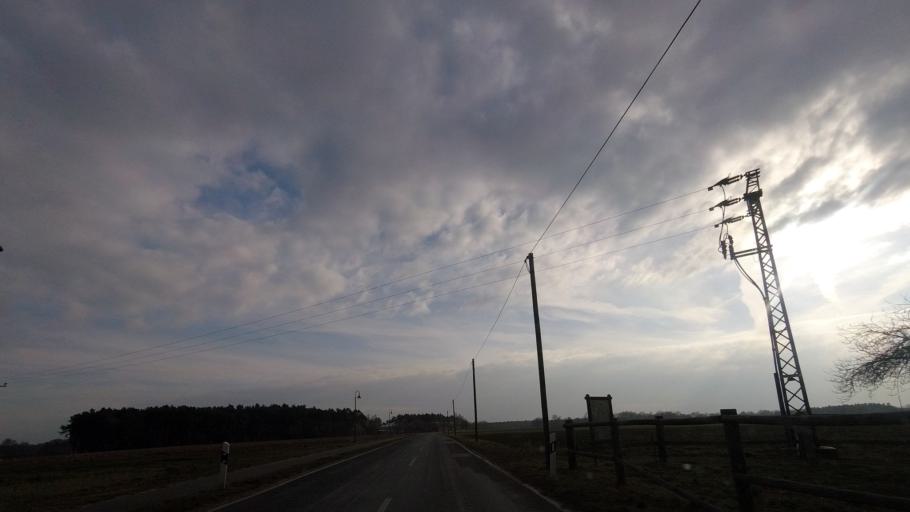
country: DE
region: Brandenburg
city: Belzig
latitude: 52.1694
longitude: 12.6800
